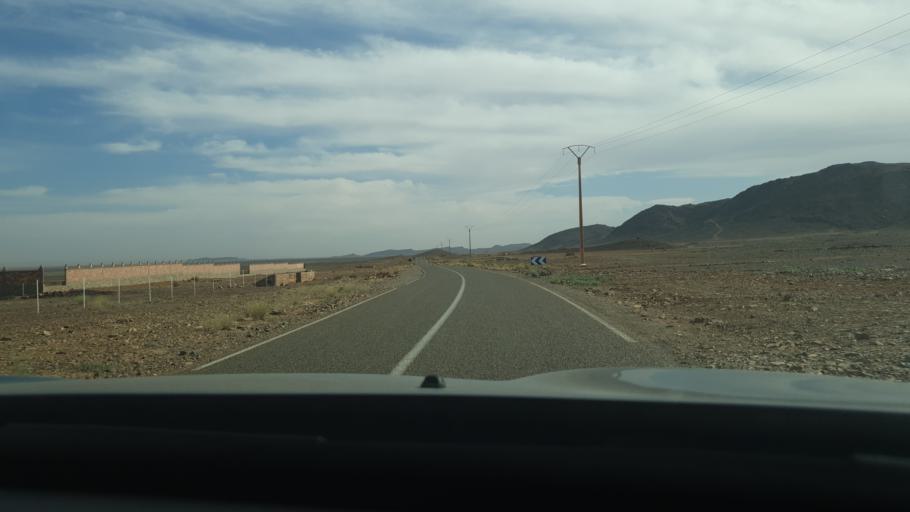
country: MA
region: Meknes-Tafilalet
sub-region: Errachidia
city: Fezna
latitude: 31.5286
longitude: -4.6365
